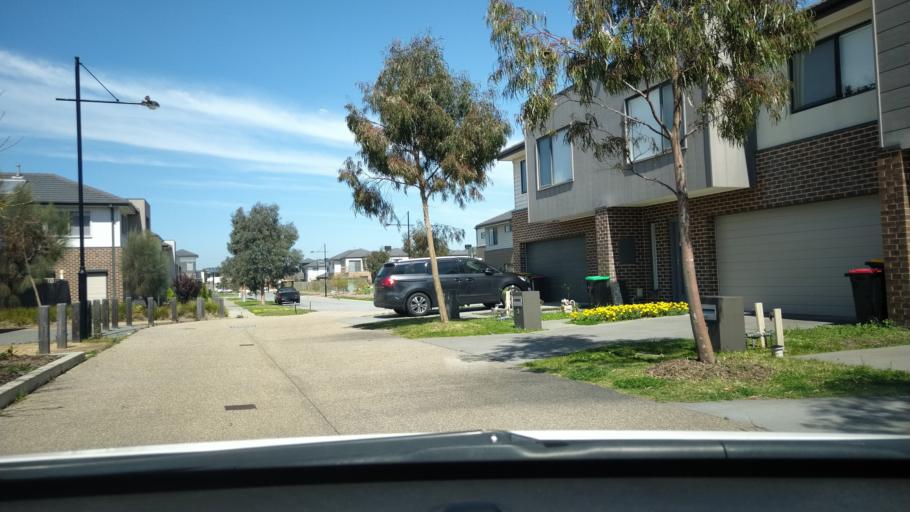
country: AU
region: Victoria
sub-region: Greater Dandenong
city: Keysborough
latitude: -38.0000
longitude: 145.1726
